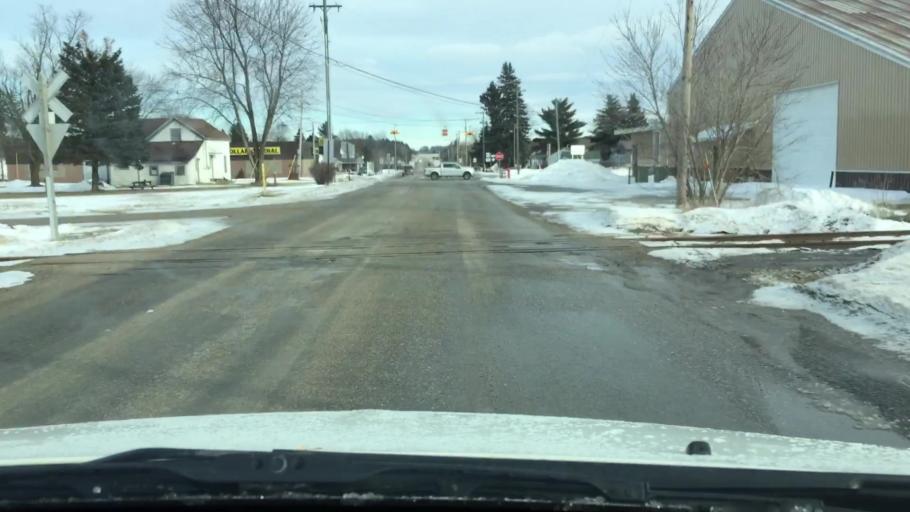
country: US
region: Michigan
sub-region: Wexford County
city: Manton
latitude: 44.4037
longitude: -85.3996
